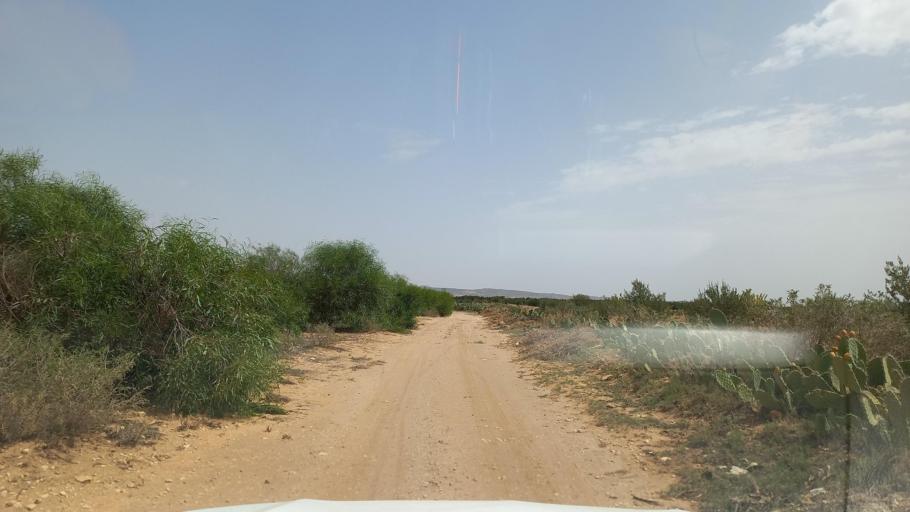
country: TN
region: Al Qasrayn
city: Kasserine
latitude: 35.2929
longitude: 9.0149
